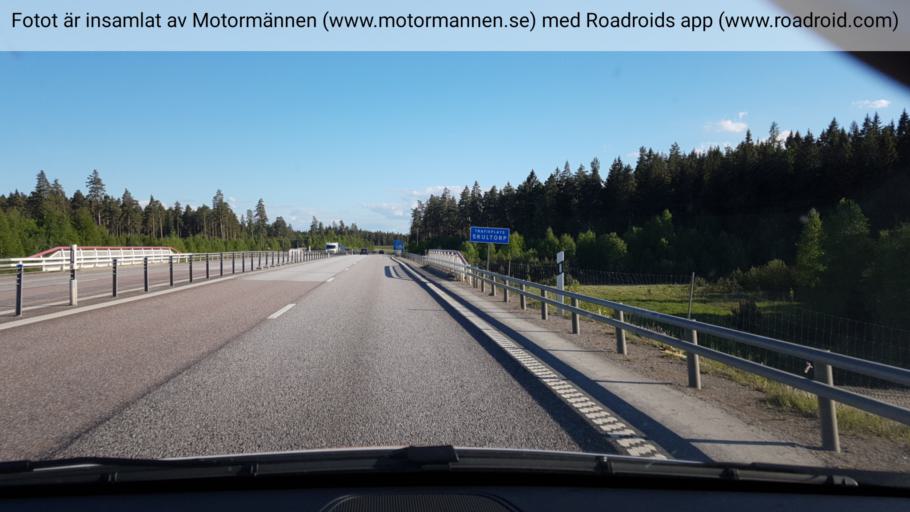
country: SE
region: Vaestra Goetaland
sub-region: Skovde Kommun
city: Skultorp
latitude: 58.3480
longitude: 13.8652
